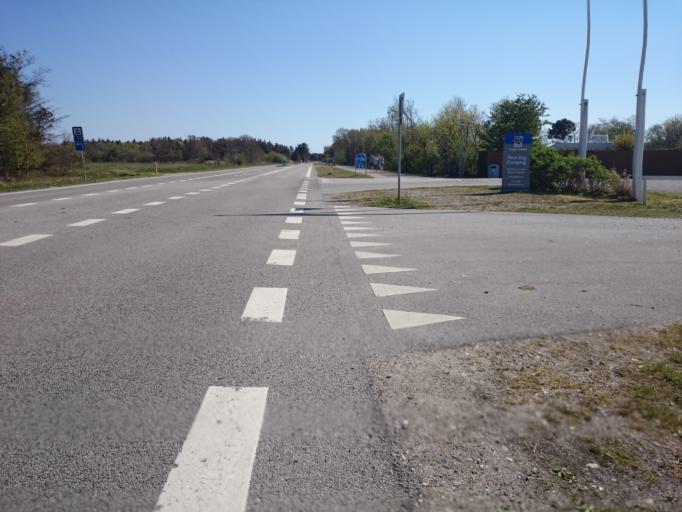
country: DK
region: North Denmark
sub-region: Frederikshavn Kommune
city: Skagen
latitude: 57.7348
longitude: 10.6040
